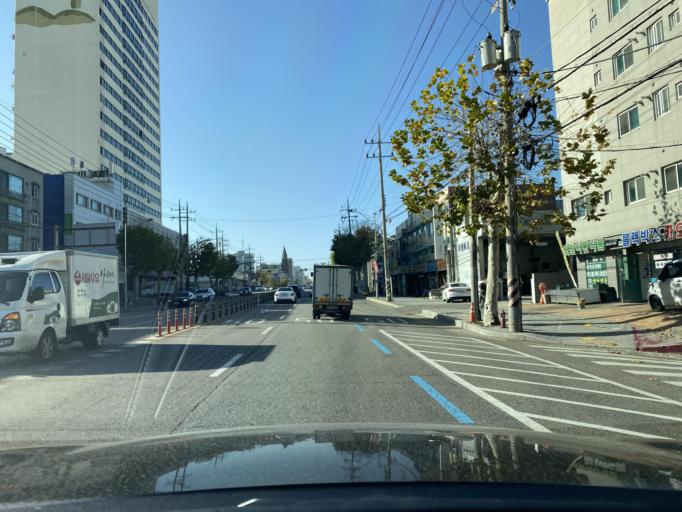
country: KR
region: Incheon
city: Incheon
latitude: 37.4870
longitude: 126.7362
